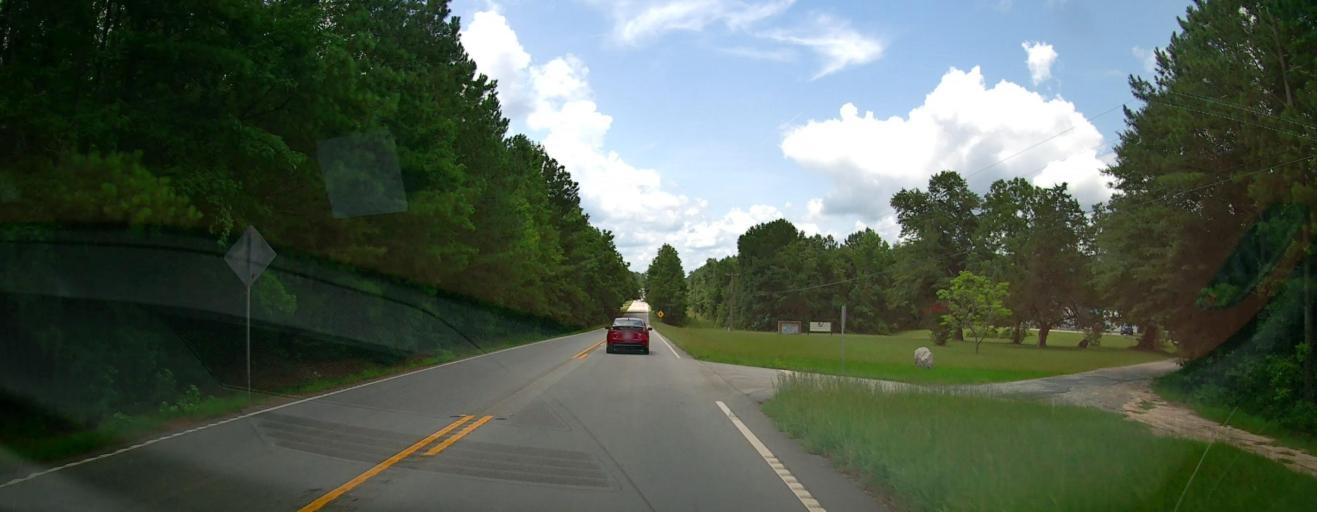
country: US
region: Georgia
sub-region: Meriwether County
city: Greenville
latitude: 32.9906
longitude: -84.6238
